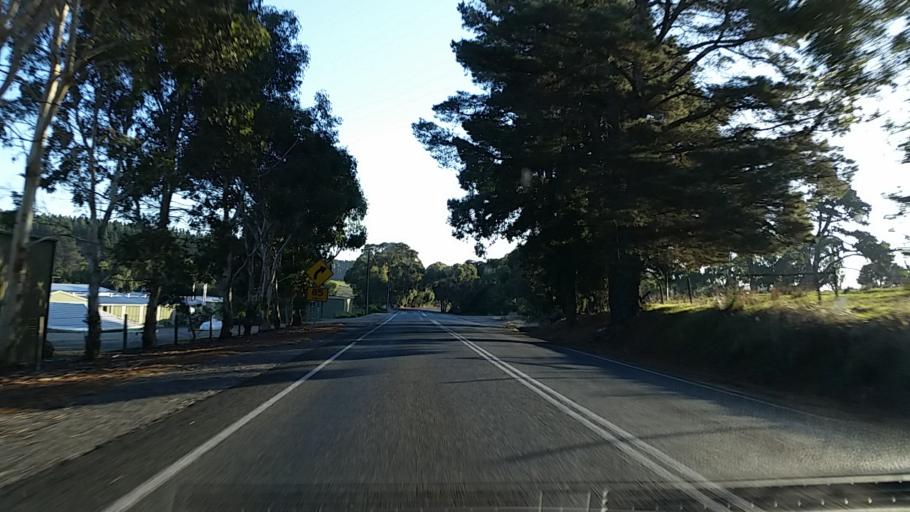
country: AU
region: South Australia
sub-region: Alexandrina
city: Mount Compass
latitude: -35.3489
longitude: 138.6371
